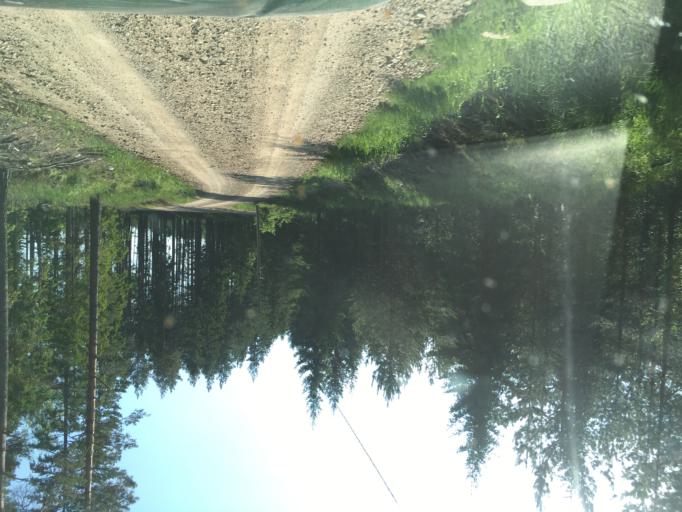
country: LV
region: Dundaga
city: Dundaga
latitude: 57.6121
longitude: 22.5050
